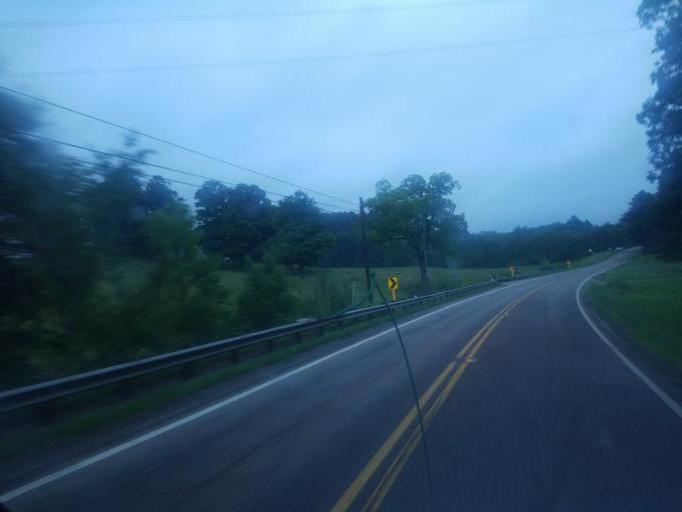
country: US
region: Ohio
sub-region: Carroll County
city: Carrollton
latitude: 40.5802
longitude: -81.0376
